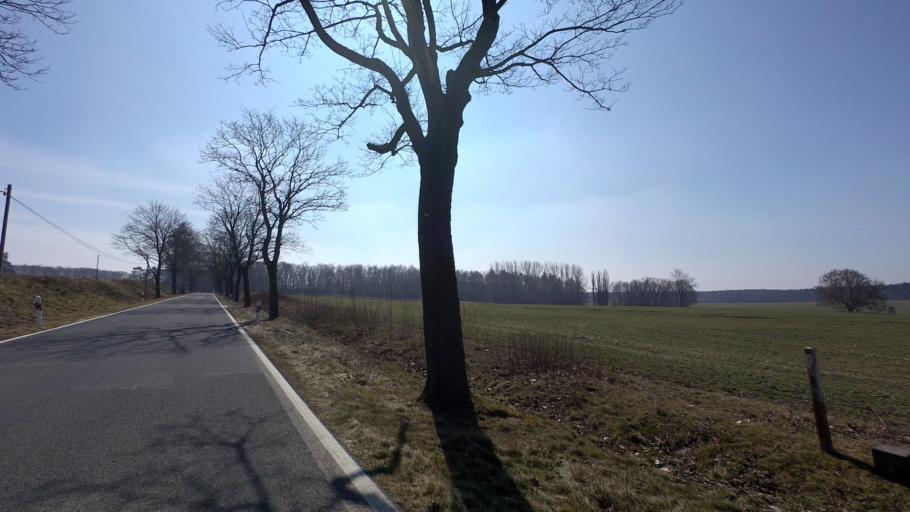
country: DE
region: Brandenburg
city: Wiesenburg
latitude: 52.0271
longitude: 12.5263
